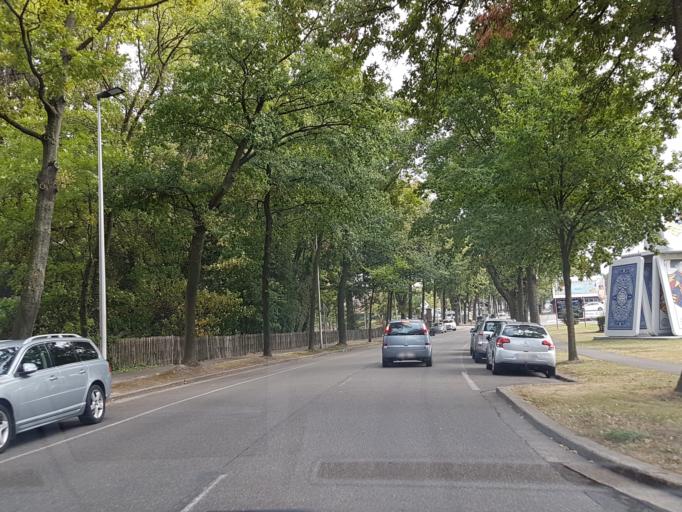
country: BE
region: Flanders
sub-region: Provincie Limburg
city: Sint-Truiden
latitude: 50.8226
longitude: 5.1895
